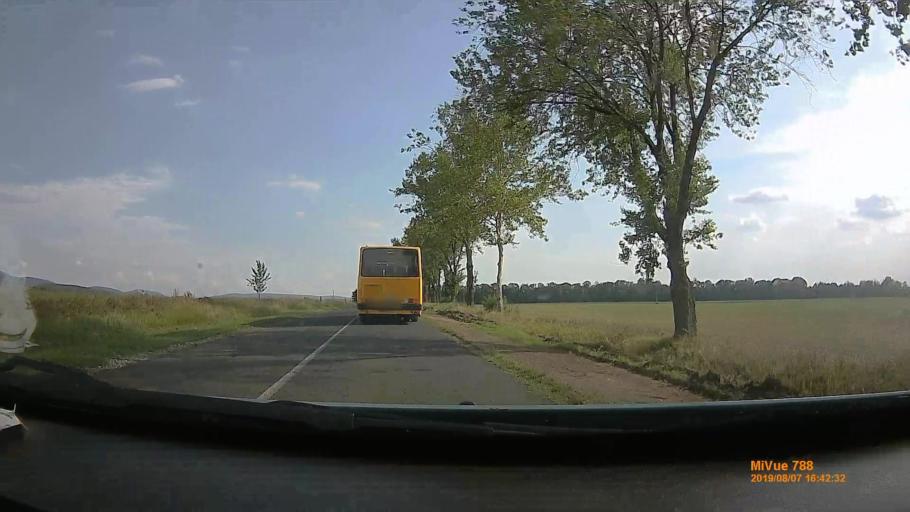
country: HU
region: Borsod-Abauj-Zemplen
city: Abaujszanto
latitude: 48.3684
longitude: 21.2157
